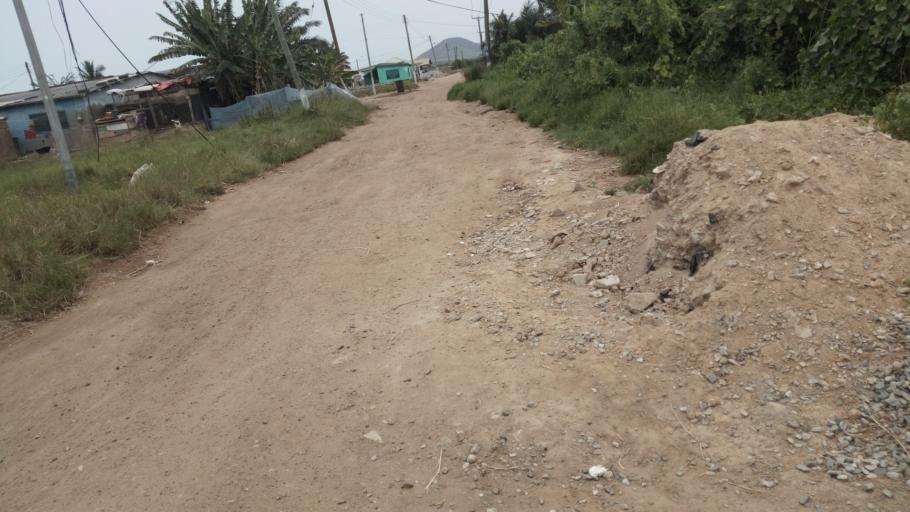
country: GH
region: Central
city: Winneba
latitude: 5.3480
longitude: -0.6325
